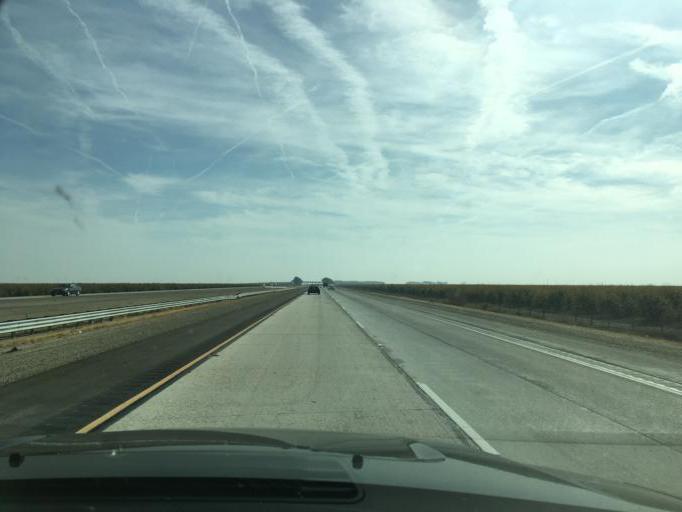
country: US
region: California
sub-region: Kern County
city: Lost Hills
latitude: 35.5862
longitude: -119.6269
